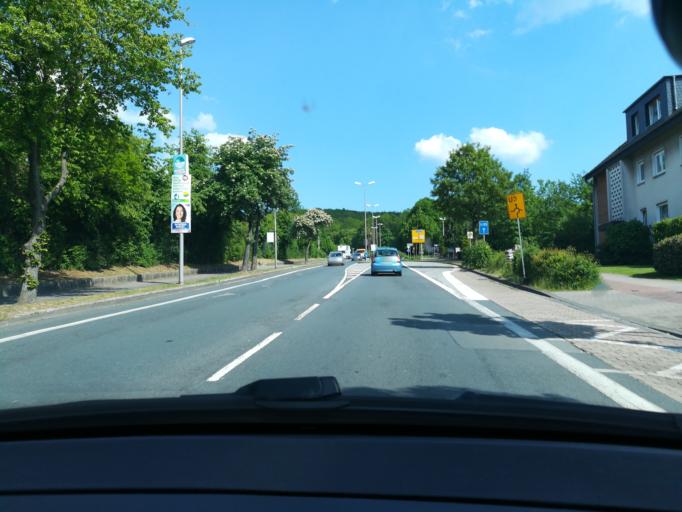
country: DE
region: North Rhine-Westphalia
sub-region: Regierungsbezirk Detmold
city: Herford
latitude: 52.1212
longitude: 8.7035
